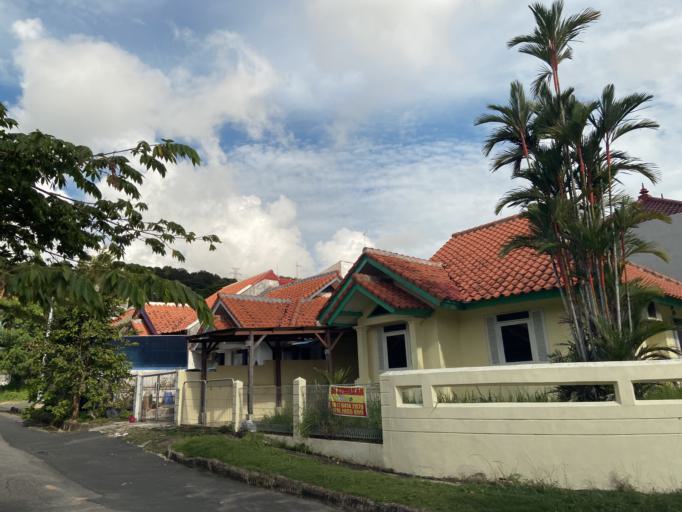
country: SG
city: Singapore
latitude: 1.1125
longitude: 104.0221
